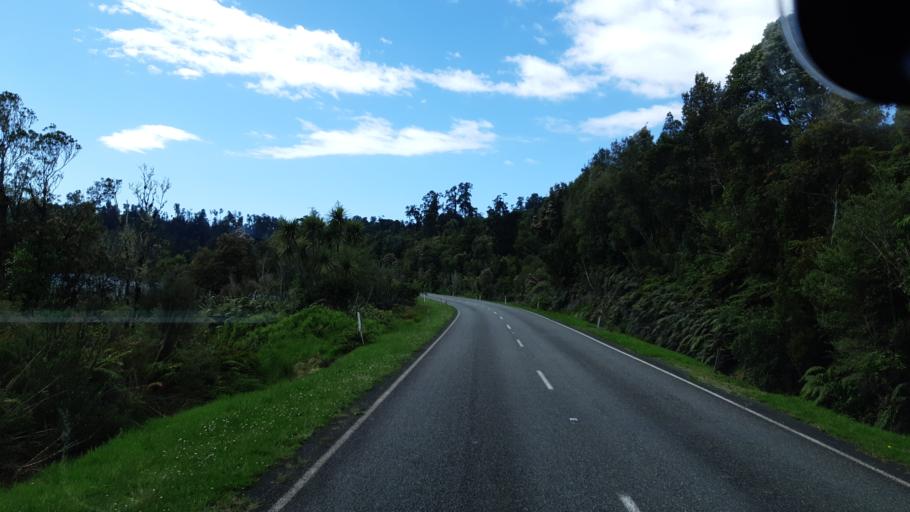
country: NZ
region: West Coast
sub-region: Westland District
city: Hokitika
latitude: -43.0522
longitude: 170.6376
